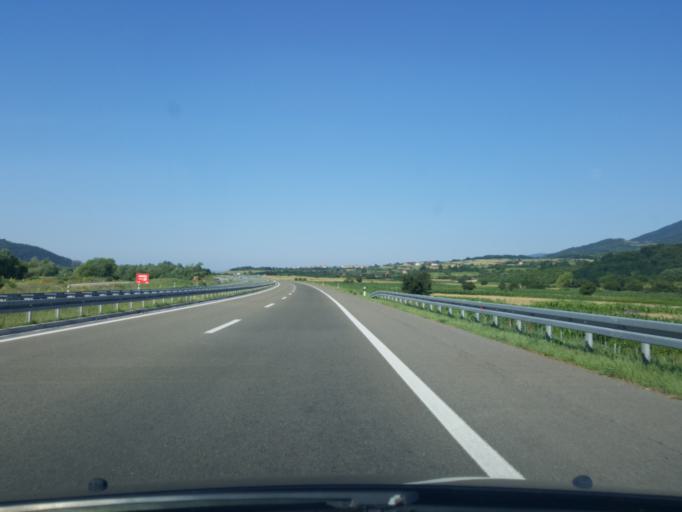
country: RS
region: Central Serbia
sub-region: Pcinjski Okrug
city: Vranjska Banja
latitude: 42.5803
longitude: 21.9912
